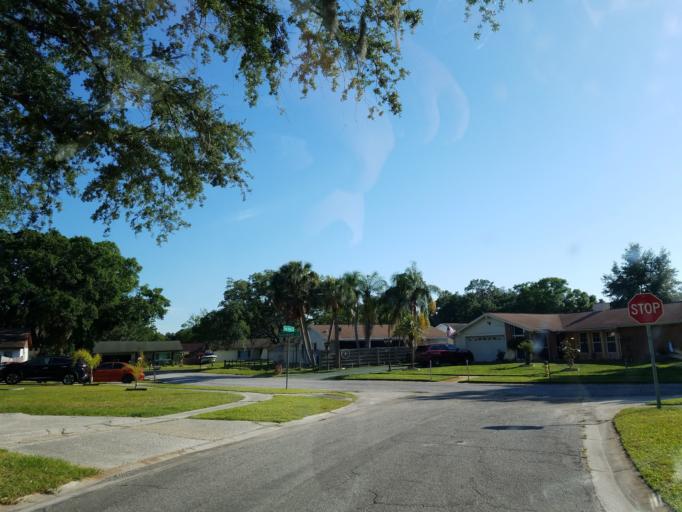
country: US
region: Florida
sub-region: Hillsborough County
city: Riverview
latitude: 27.8874
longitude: -82.2946
